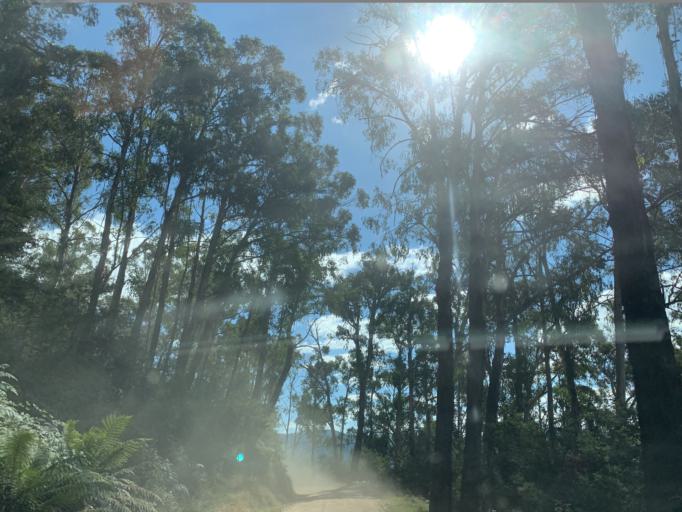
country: AU
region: Victoria
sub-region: Mansfield
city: Mansfield
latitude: -37.0980
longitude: 146.4863
